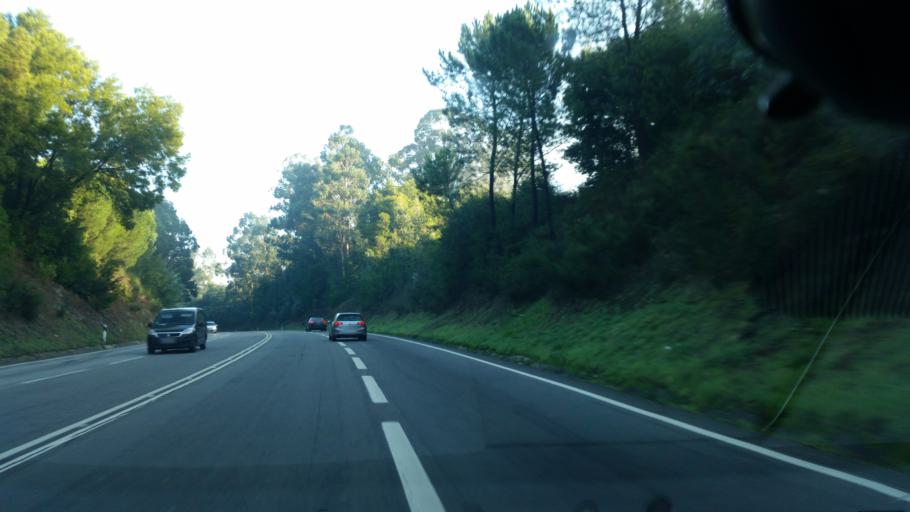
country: PT
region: Porto
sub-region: Santo Tirso
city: Sao Miguel do Couto
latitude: 41.3344
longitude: -8.4676
